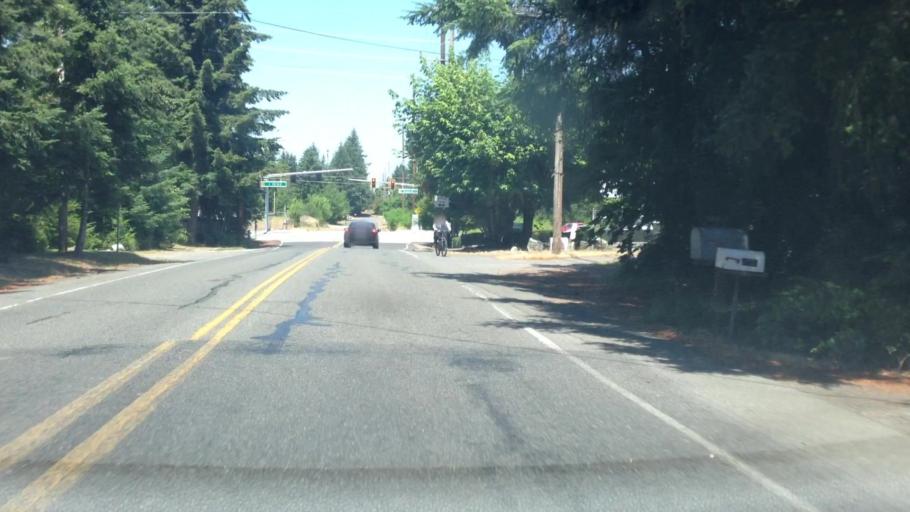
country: US
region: Washington
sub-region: Pierce County
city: Puyallup
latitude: 47.1539
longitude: -122.3148
